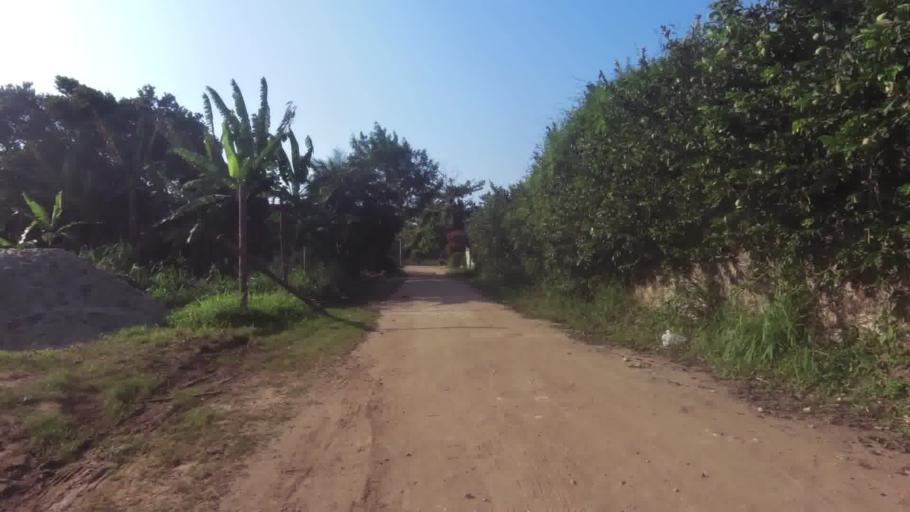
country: BR
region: Espirito Santo
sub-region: Piuma
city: Piuma
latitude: -20.8538
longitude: -40.7546
